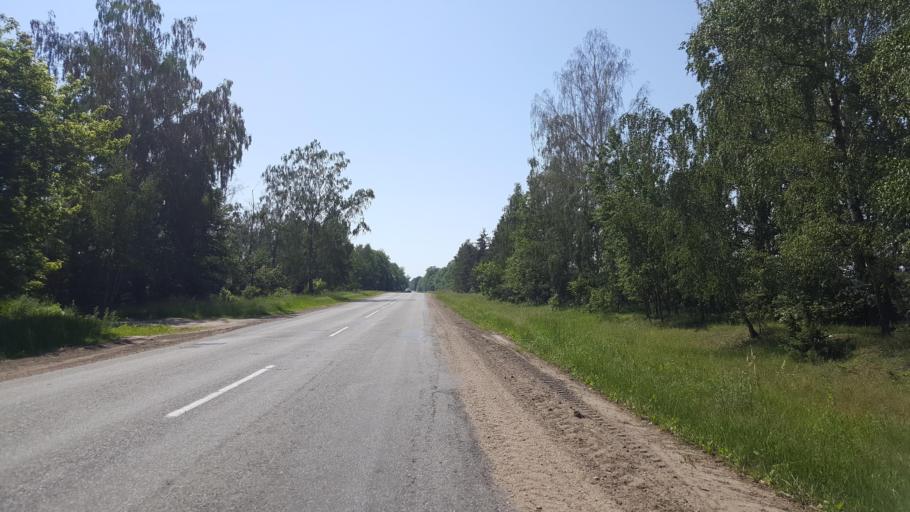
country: BY
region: Brest
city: Zhabinka
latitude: 52.2415
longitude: 23.9764
